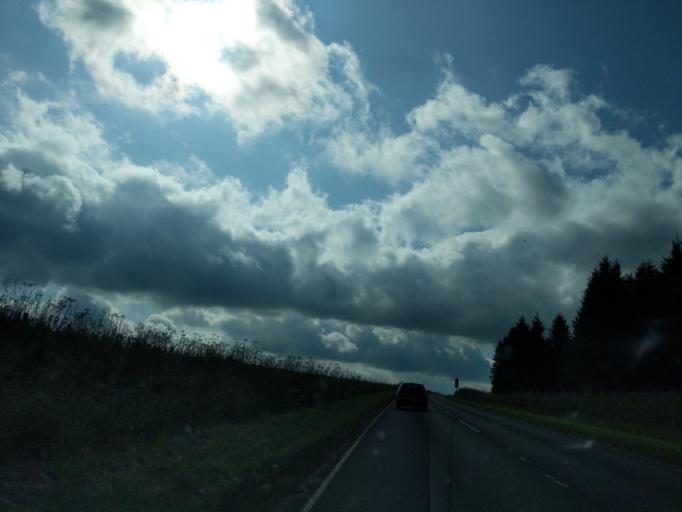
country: GB
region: Scotland
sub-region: Midlothian
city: Penicuik
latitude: 55.7838
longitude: -3.2199
